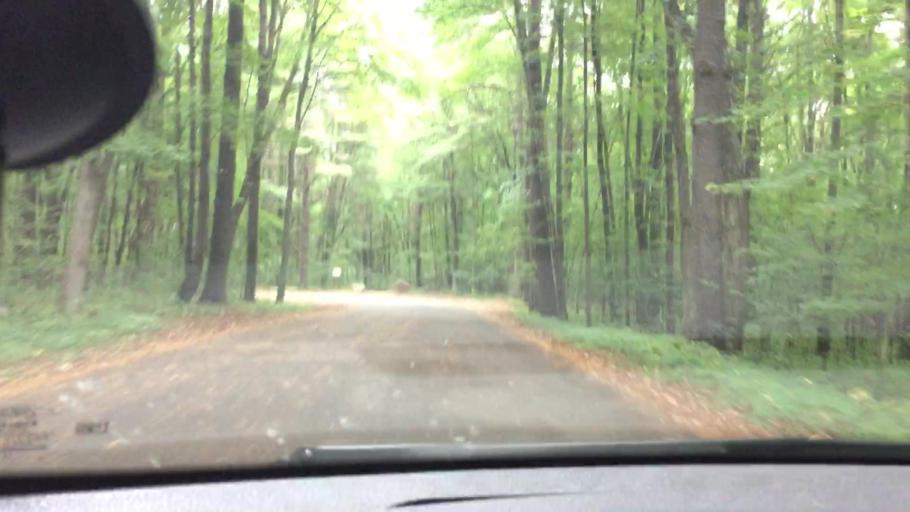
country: US
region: Wisconsin
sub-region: Chippewa County
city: Chippewa Falls
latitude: 44.9570
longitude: -91.4019
